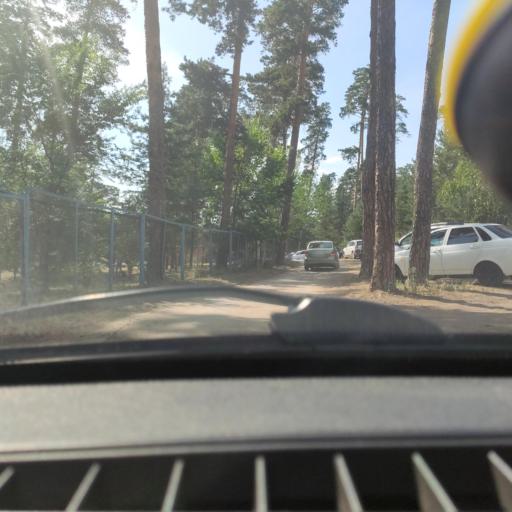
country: RU
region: Samara
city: Tol'yatti
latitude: 53.4737
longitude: 49.3380
